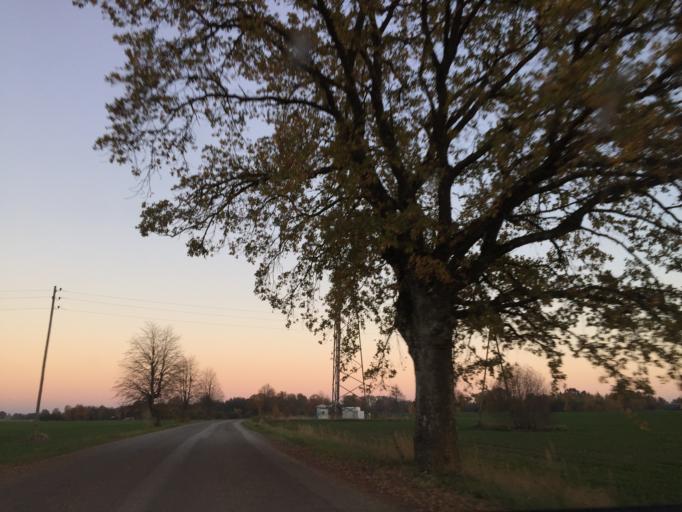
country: LT
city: Vieksniai
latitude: 56.3867
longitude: 22.6128
